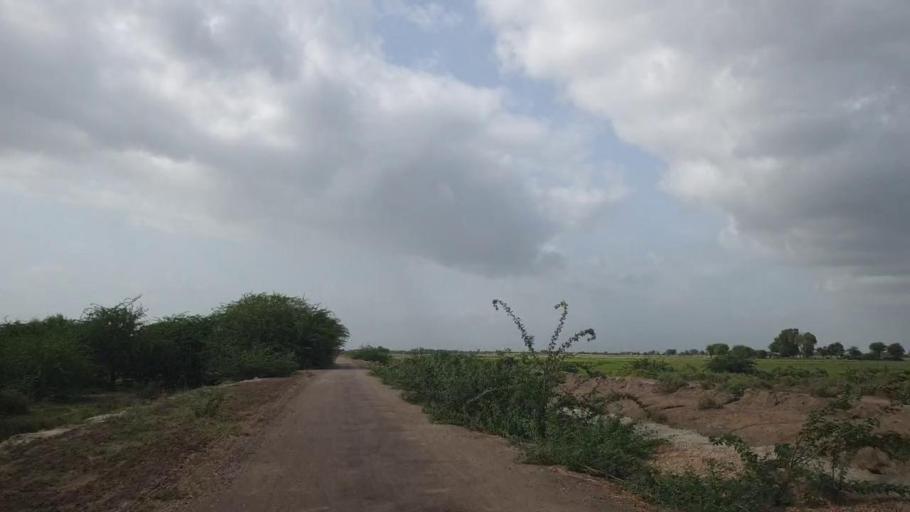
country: PK
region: Sindh
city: Kadhan
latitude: 24.5614
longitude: 69.0638
